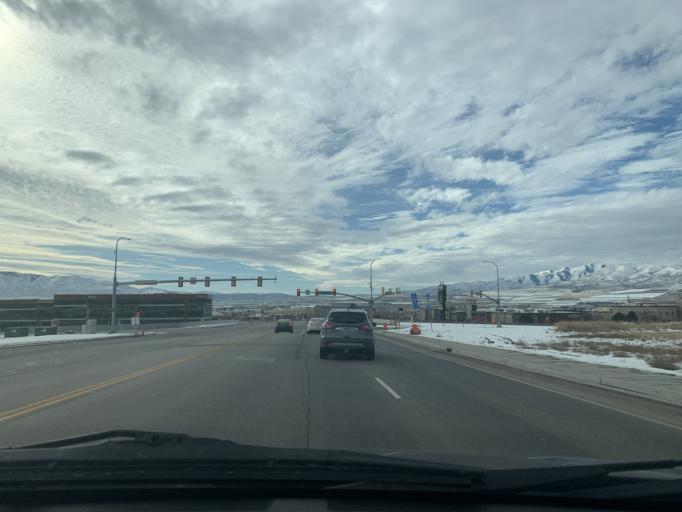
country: US
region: Utah
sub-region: Utah County
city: Lehi
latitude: 40.4252
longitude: -111.8812
